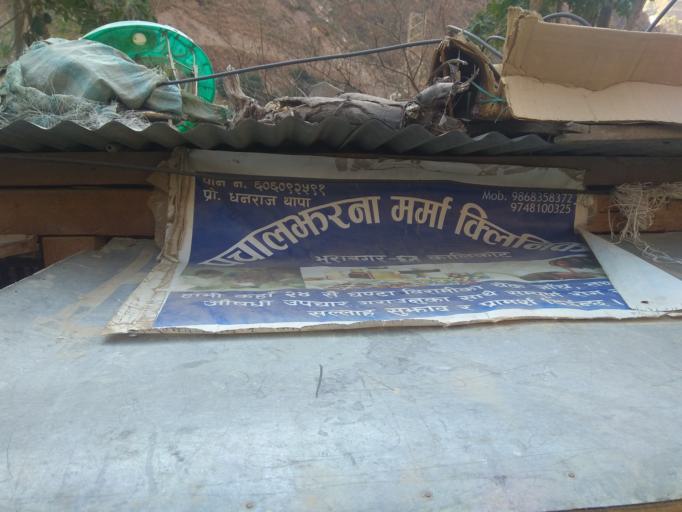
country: NP
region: Mid Western
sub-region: Bheri Zone
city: Dailekh
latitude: 29.2713
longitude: 81.7140
